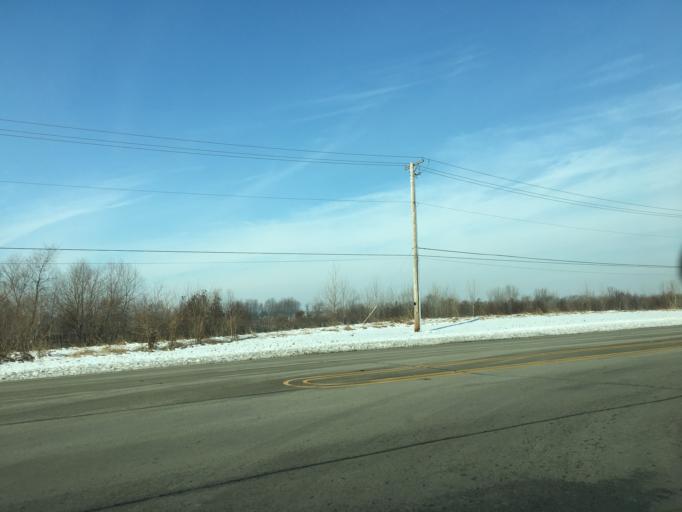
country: US
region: Illinois
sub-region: Will County
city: Plainfield
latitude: 41.6564
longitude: -88.1784
